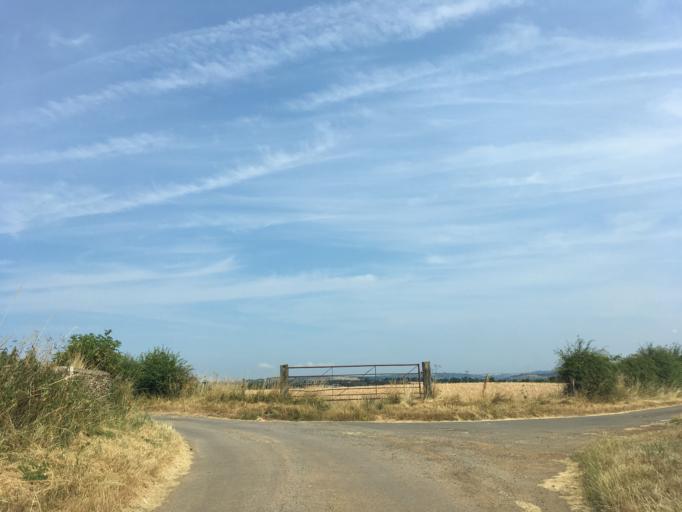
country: GB
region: England
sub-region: Gloucestershire
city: Nailsworth
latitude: 51.6653
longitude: -2.2411
